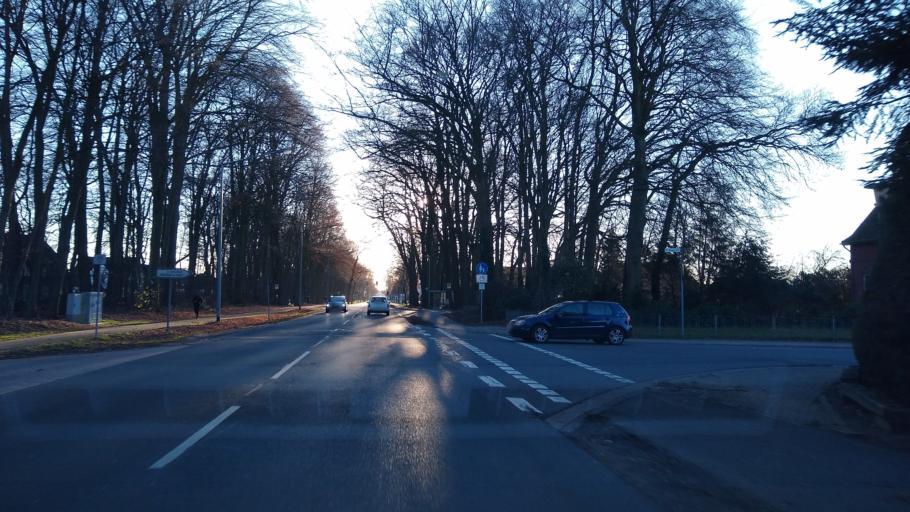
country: DE
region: Lower Saxony
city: Cloppenburg
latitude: 52.8571
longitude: 8.0574
